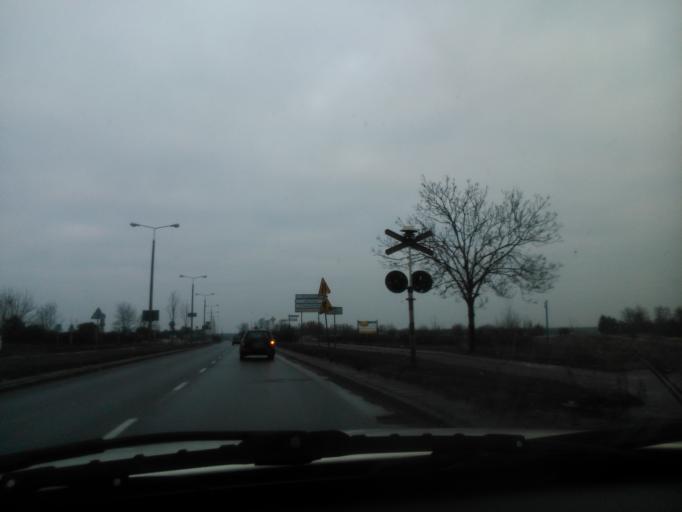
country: PL
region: Kujawsko-Pomorskie
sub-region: Torun
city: Torun
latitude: 53.0391
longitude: 18.6137
